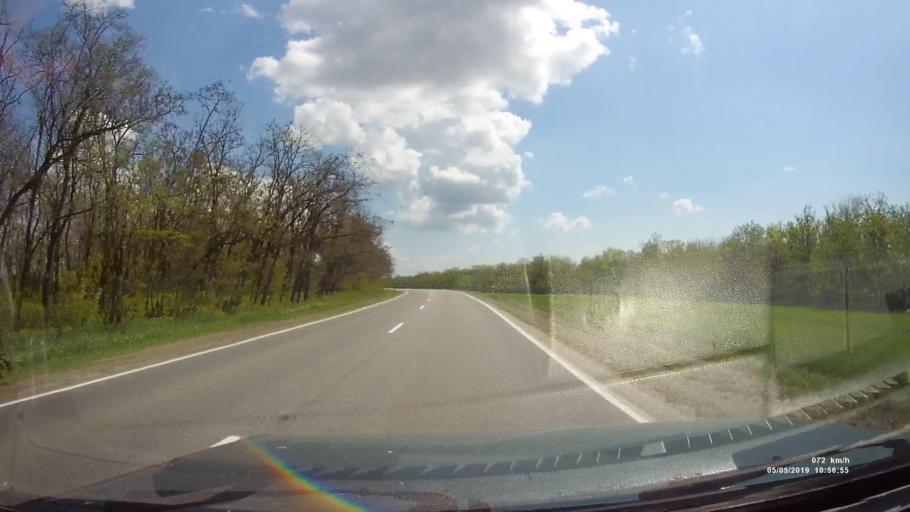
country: RU
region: Rostov
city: Ust'-Donetskiy
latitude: 47.6709
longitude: 40.8276
